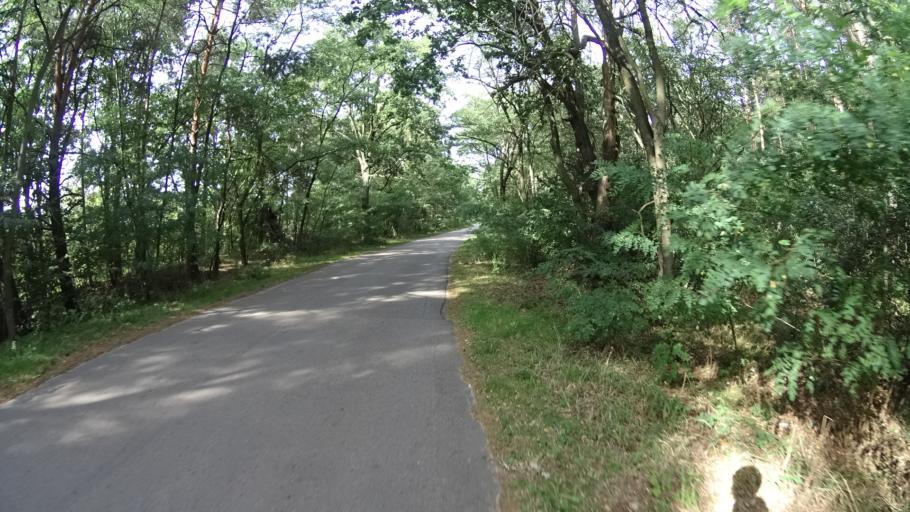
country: PL
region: Masovian Voivodeship
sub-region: Powiat legionowski
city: Serock
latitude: 52.4911
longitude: 21.0870
